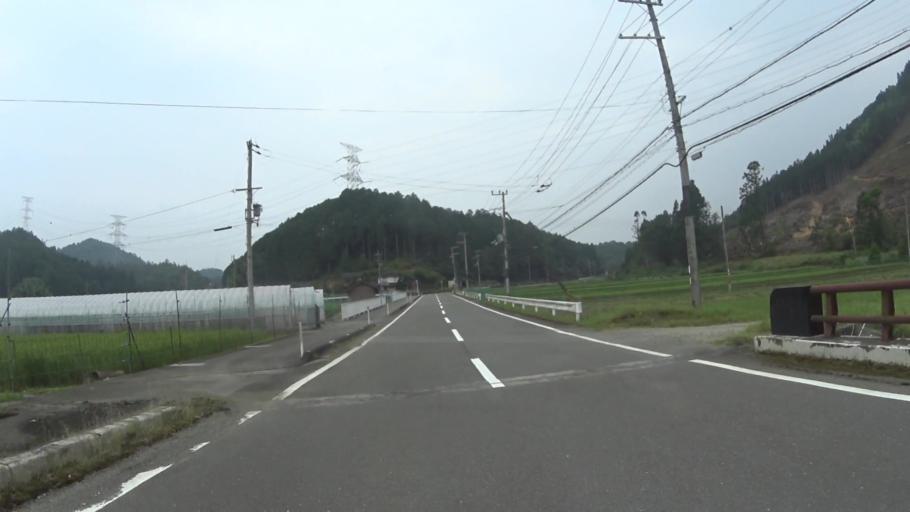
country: JP
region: Kyoto
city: Kameoka
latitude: 35.1718
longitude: 135.6132
